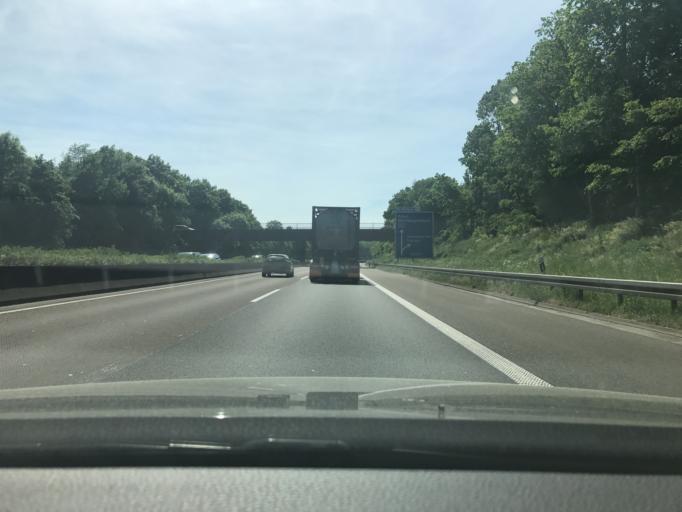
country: DE
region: North Rhine-Westphalia
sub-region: Regierungsbezirk Dusseldorf
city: Monchengladbach
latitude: 51.2280
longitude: 6.4420
